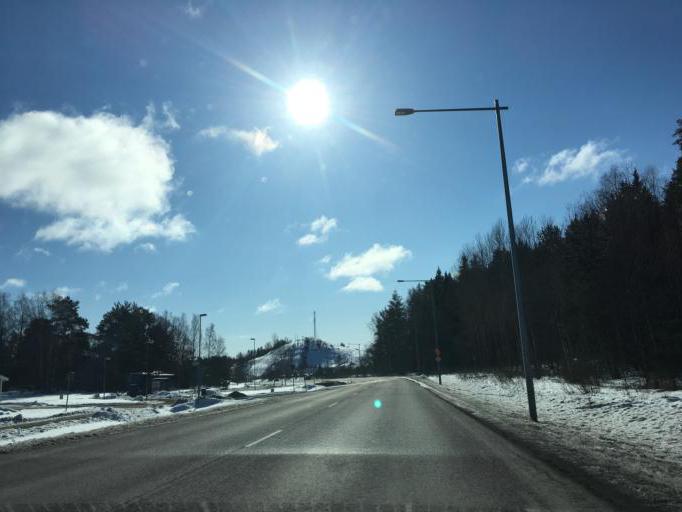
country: SE
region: Vaestmanland
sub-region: Vasteras
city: Vasteras
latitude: 59.6306
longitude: 16.4787
